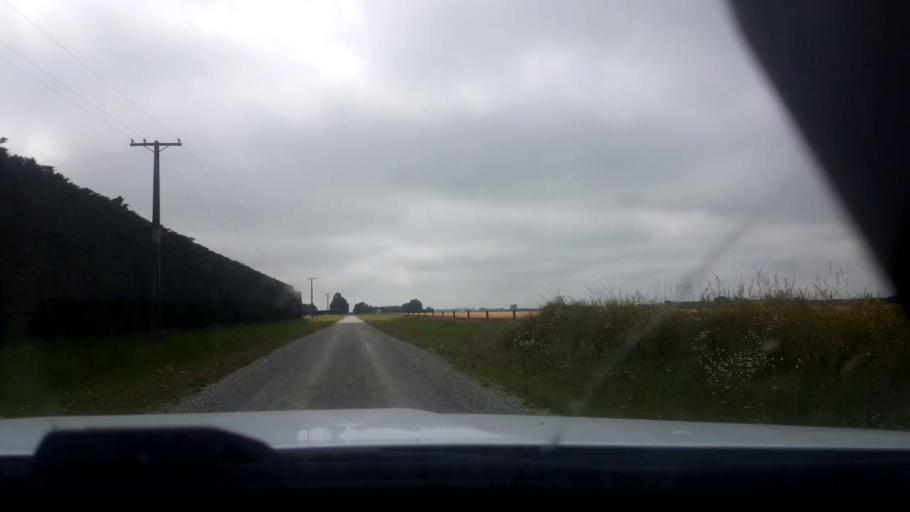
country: NZ
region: Canterbury
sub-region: Timaru District
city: Pleasant Point
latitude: -44.2867
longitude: 171.1971
